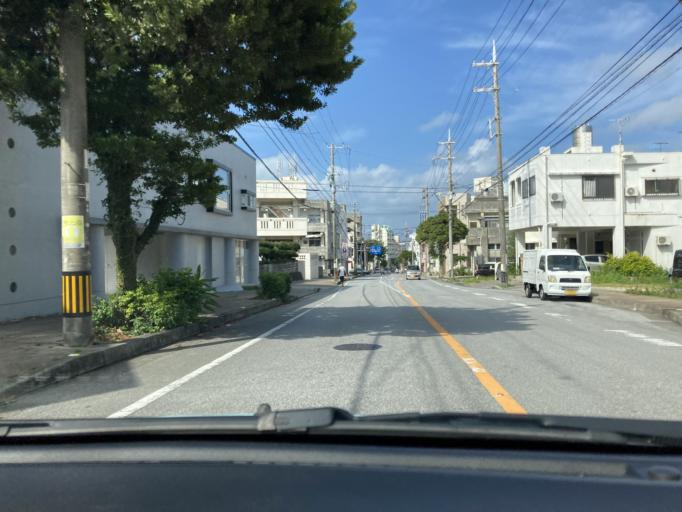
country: JP
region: Okinawa
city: Chatan
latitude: 26.2895
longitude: 127.7819
